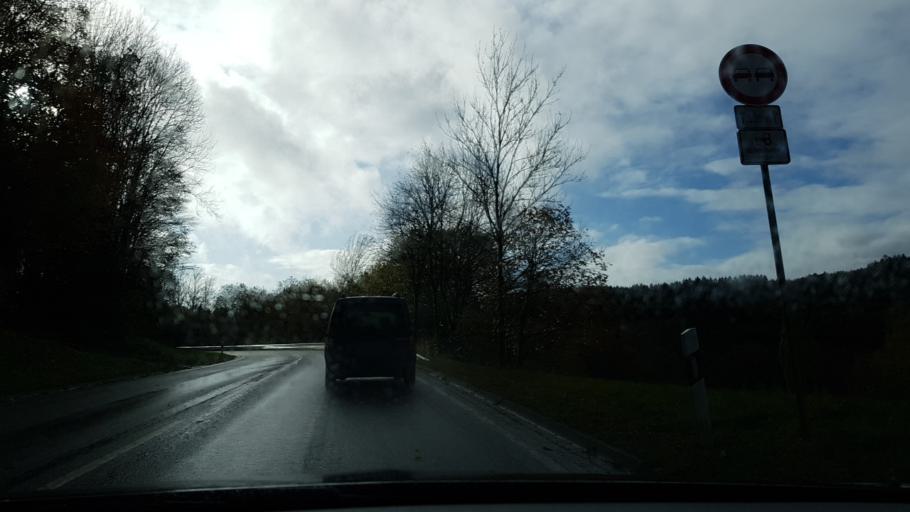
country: DE
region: Rheinland-Pfalz
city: Quiddelbach
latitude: 50.3475
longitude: 6.9363
